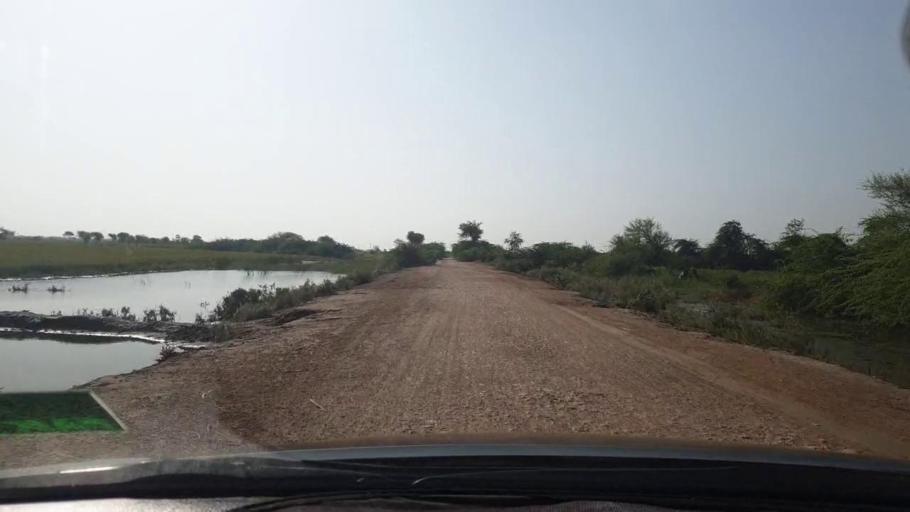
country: PK
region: Sindh
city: Tando Bago
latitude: 24.7220
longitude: 68.9587
